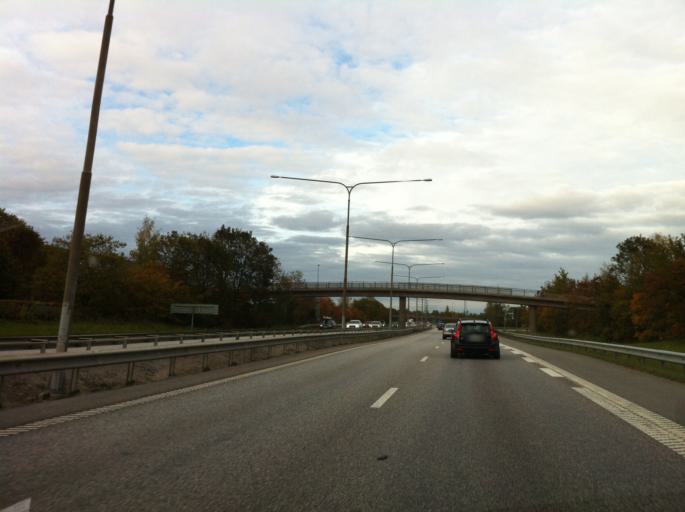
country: SE
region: OErebro
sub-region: Orebro Kommun
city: Orebro
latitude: 59.2657
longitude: 15.1736
